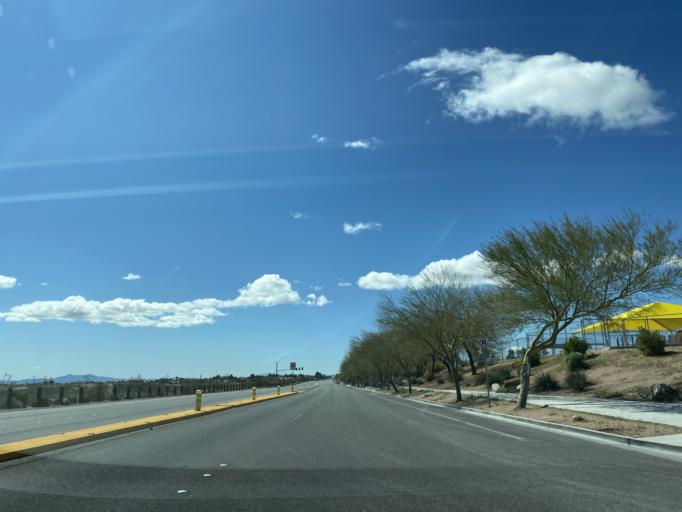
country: US
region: Nevada
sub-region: Clark County
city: North Las Vegas
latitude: 36.3243
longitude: -115.2786
